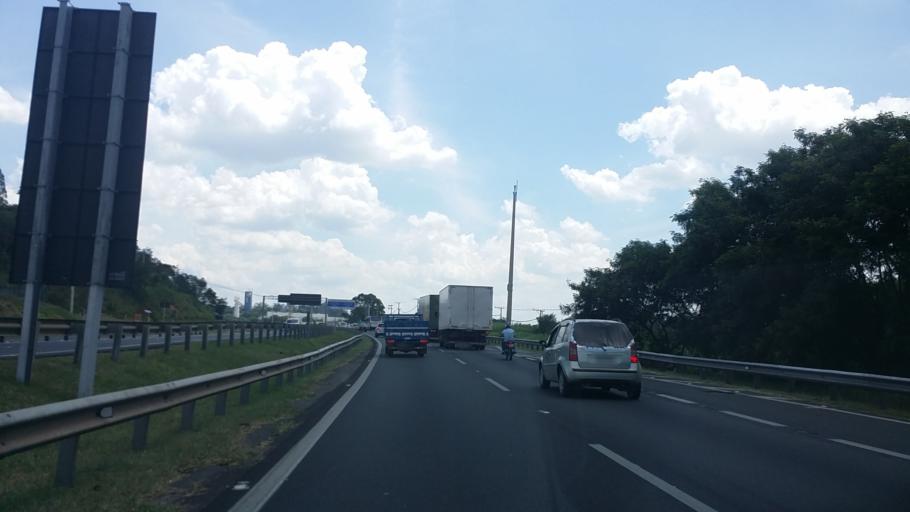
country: BR
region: Sao Paulo
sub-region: Jundiai
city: Jundiai
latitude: -23.1720
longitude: -46.9461
